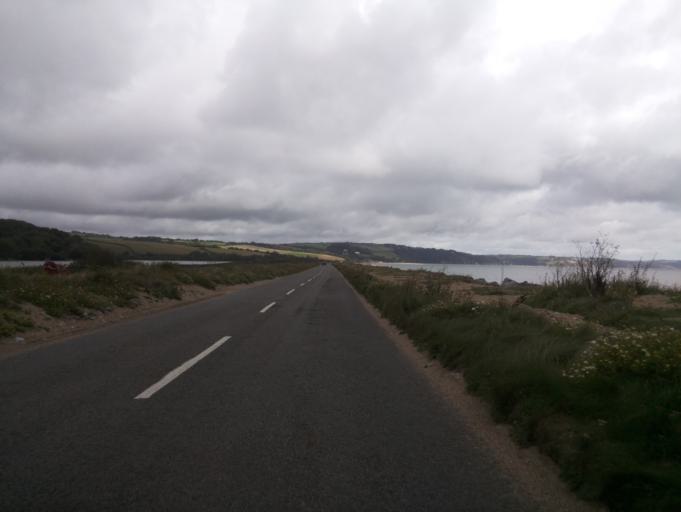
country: GB
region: England
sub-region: Devon
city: Dartmouth
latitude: 50.2759
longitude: -3.6498
